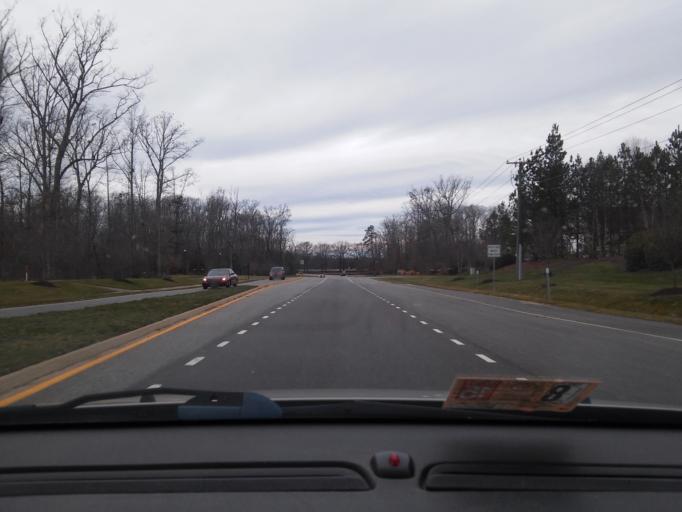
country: US
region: Virginia
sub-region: Chesterfield County
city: Bon Air
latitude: 37.5523
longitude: -77.6598
